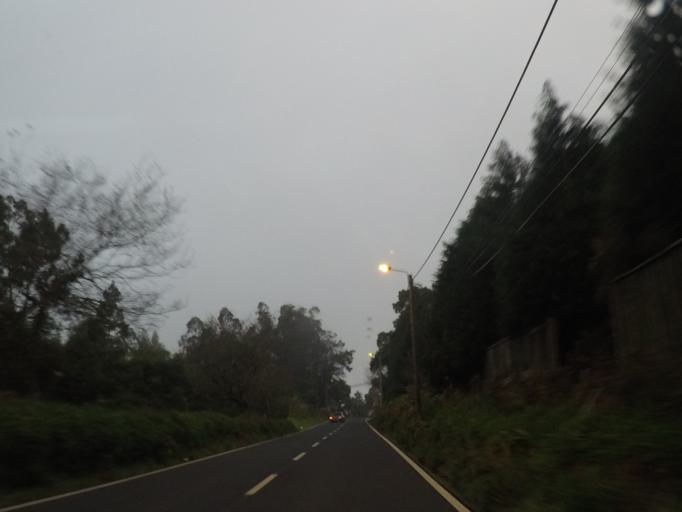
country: PT
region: Madeira
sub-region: Santa Cruz
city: Camacha
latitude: 32.7132
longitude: -16.8305
